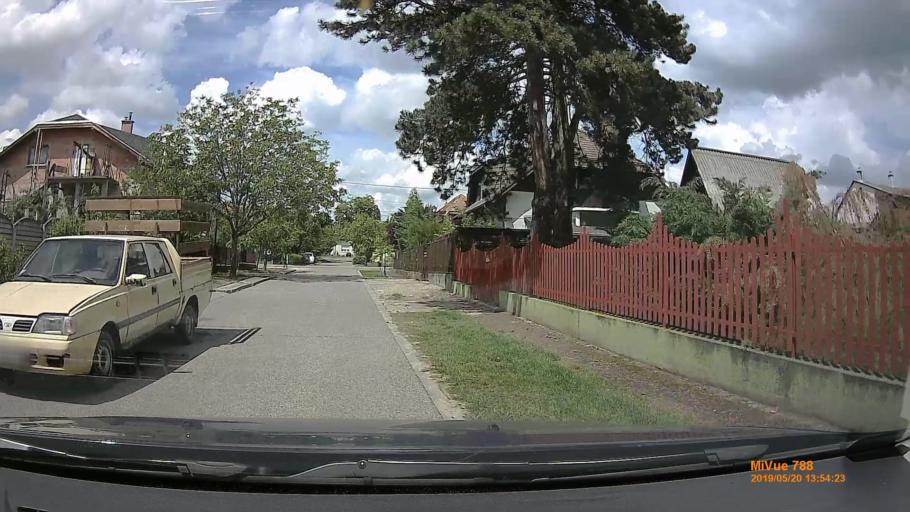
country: HU
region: Budapest
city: Budapest XVII. keruelet
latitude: 47.4905
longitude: 19.2451
